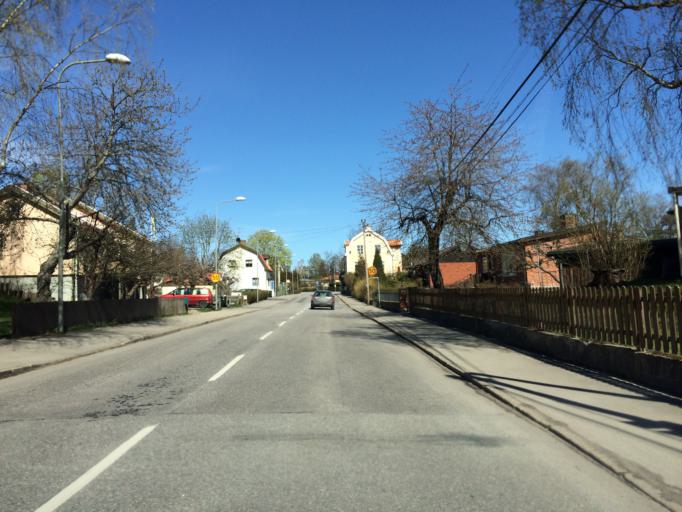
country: SE
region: Stockholm
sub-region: Huddinge Kommun
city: Segeltorp
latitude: 59.2761
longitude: 17.9613
